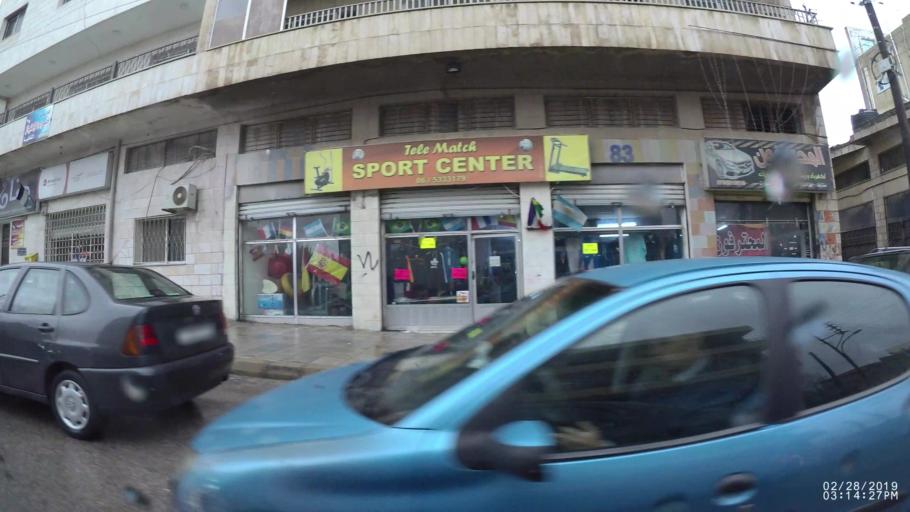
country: JO
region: Amman
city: Al Jubayhah
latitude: 32.0265
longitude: 35.8638
